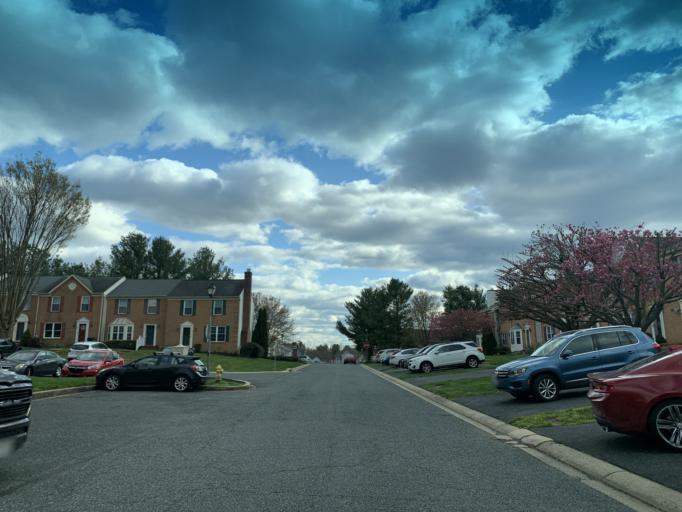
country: US
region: Maryland
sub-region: Harford County
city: South Bel Air
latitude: 39.5490
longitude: -76.3171
